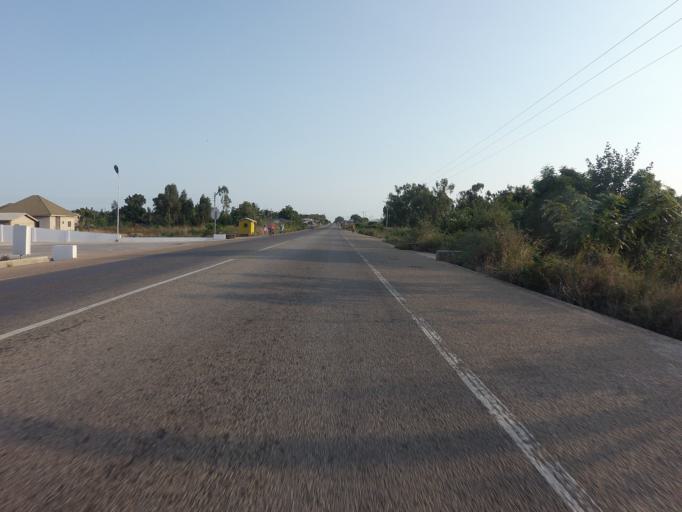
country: GH
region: Volta
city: Anloga
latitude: 6.0153
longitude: 0.5984
